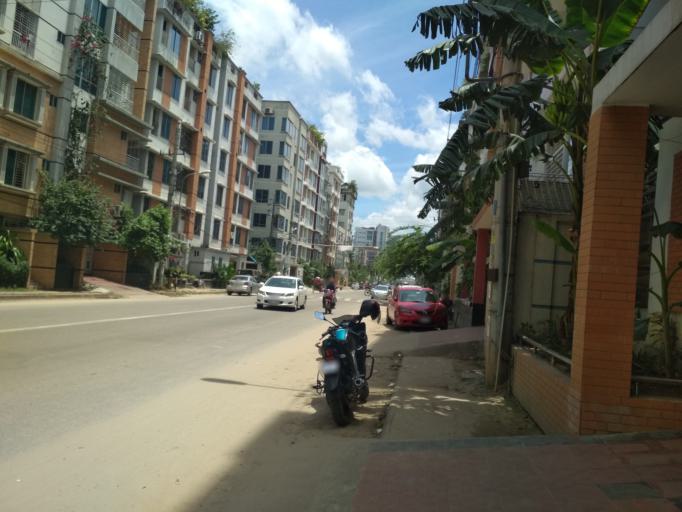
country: BD
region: Dhaka
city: Tungi
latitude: 23.8375
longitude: 90.3706
